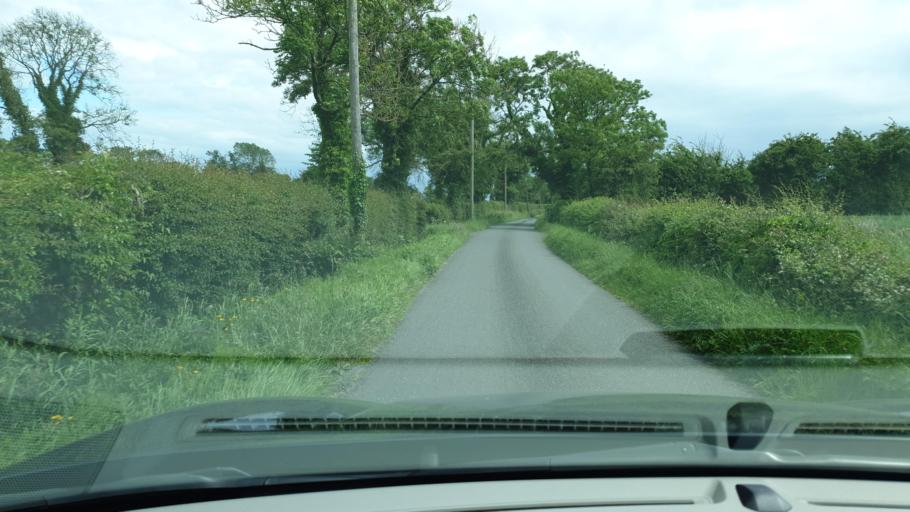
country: IE
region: Leinster
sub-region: An Mhi
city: Ratoath
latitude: 53.4608
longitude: -6.4649
